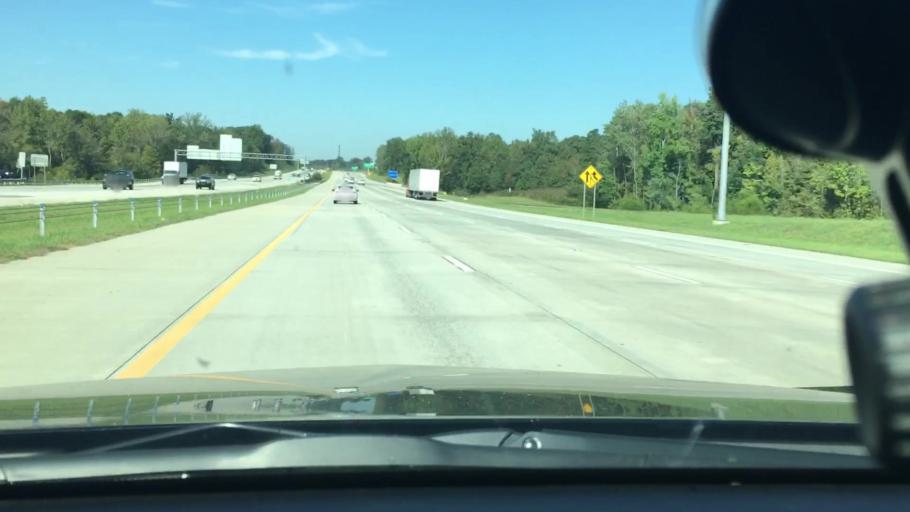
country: US
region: North Carolina
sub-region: Cabarrus County
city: Harrisburg
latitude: 35.3628
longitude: -80.7514
